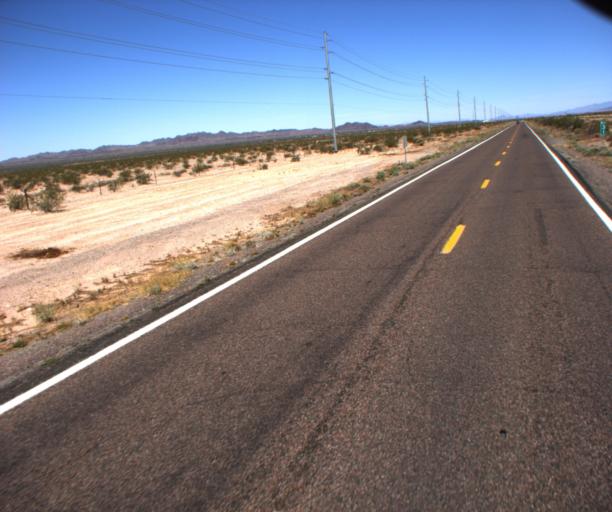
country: US
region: Arizona
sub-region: La Paz County
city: Quartzsite
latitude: 33.8904
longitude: -113.9591
